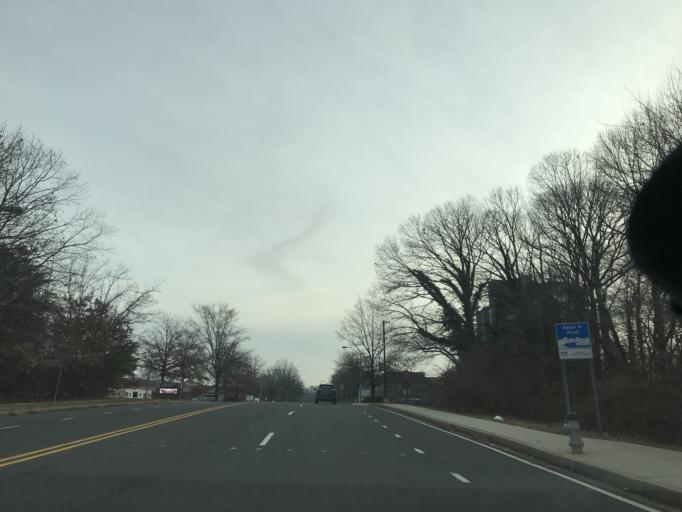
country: US
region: Maryland
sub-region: Prince George's County
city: Glenarden
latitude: 38.9466
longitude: -76.8674
